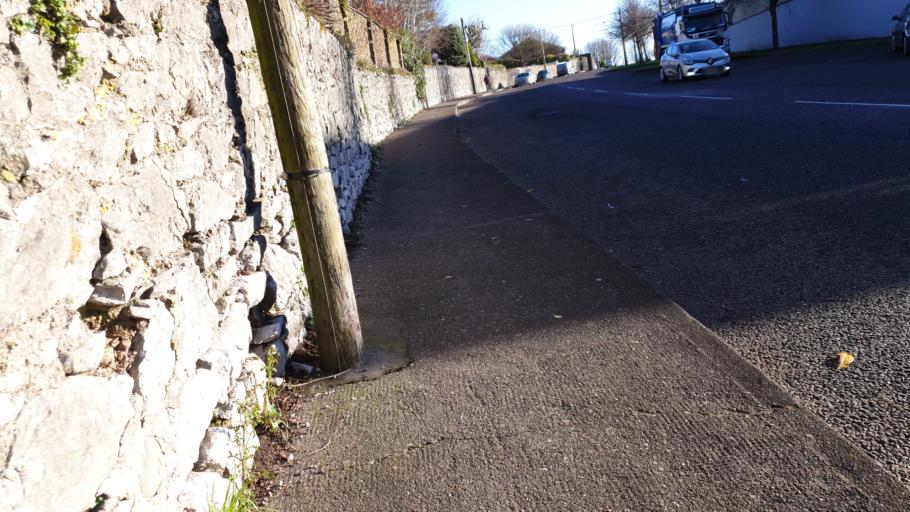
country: IE
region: Munster
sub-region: County Cork
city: Cork
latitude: 51.8921
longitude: -8.4371
